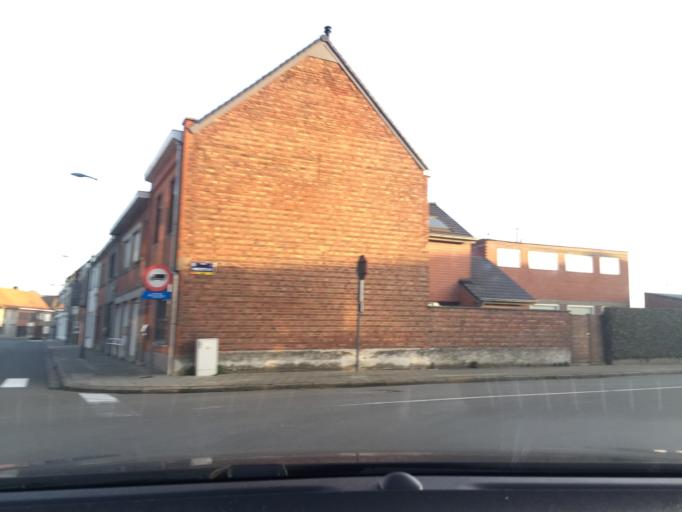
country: BE
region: Flanders
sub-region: Provincie West-Vlaanderen
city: Ardooie
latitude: 50.9730
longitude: 3.1961
